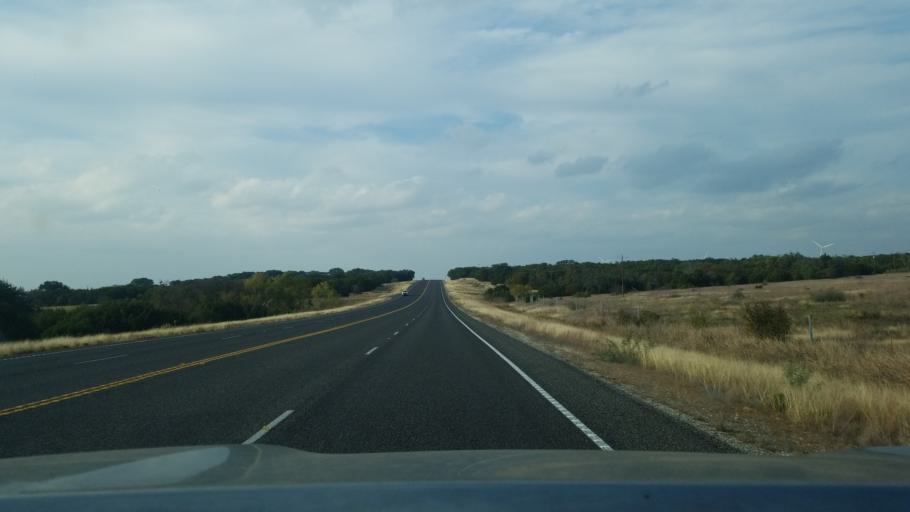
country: US
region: Texas
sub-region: Mills County
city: Goldthwaite
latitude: 31.3321
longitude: -98.4948
